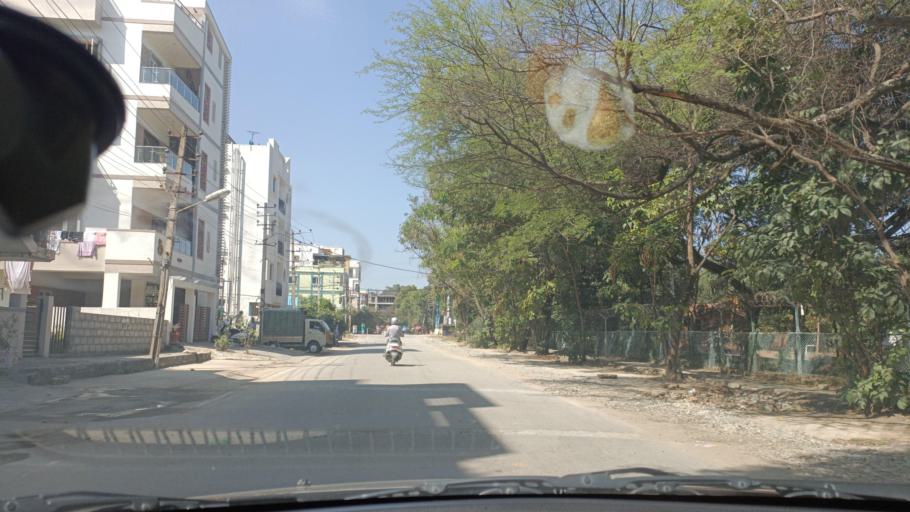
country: IN
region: Karnataka
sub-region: Bangalore Urban
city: Bangalore
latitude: 13.0331
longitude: 77.6266
